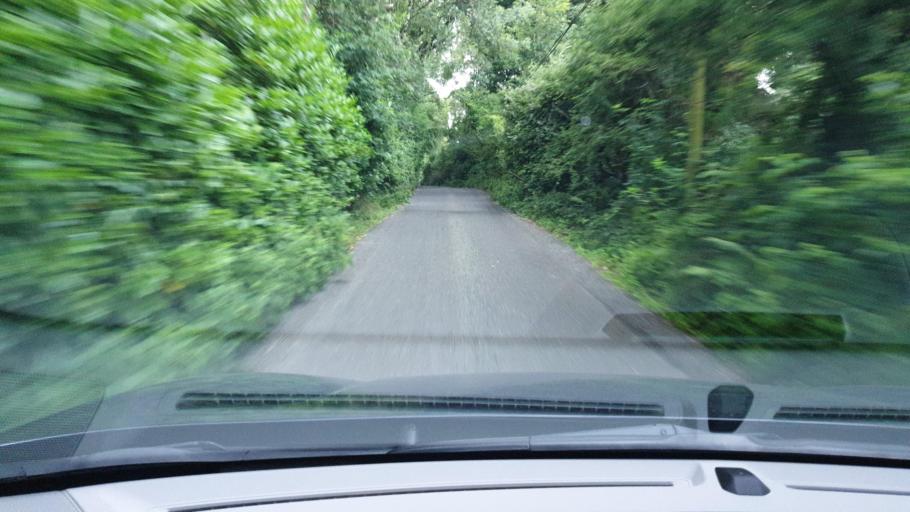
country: IE
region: Leinster
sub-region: Wicklow
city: Blessington
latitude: 53.2260
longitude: -6.5082
